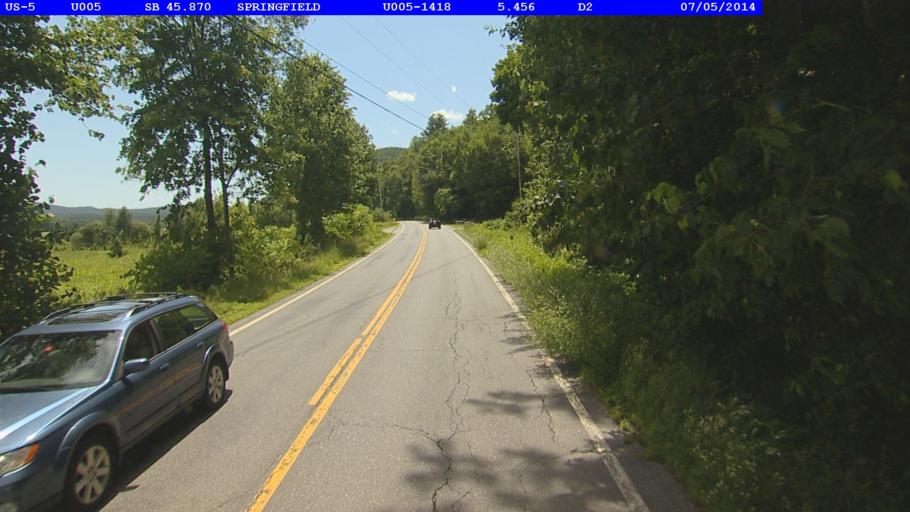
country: US
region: New Hampshire
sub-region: Sullivan County
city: Charlestown
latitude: 43.2921
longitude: -72.4122
